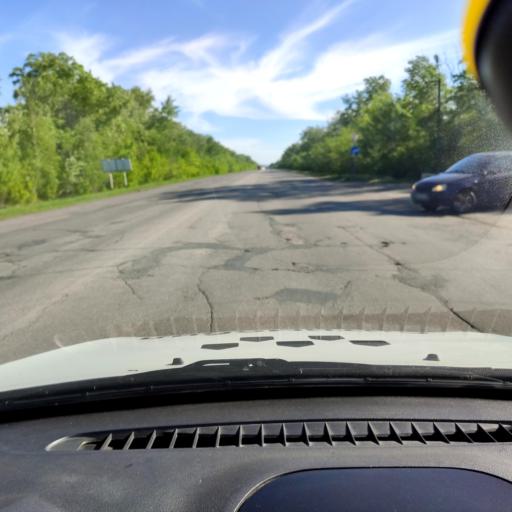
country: RU
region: Samara
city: Tol'yatti
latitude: 53.6200
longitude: 49.4143
